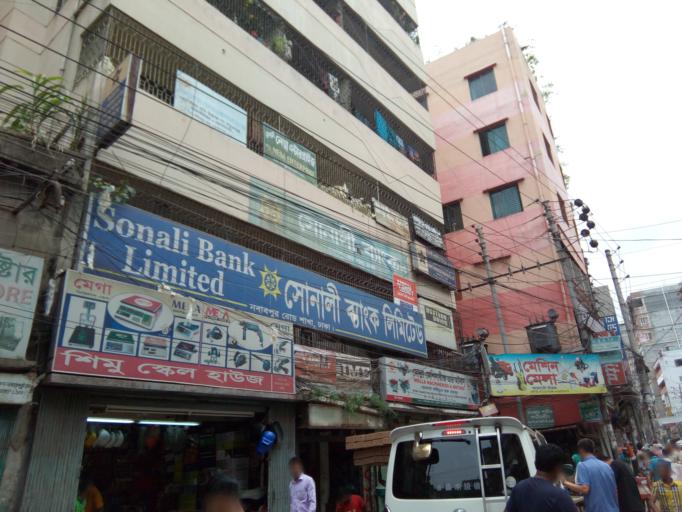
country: BD
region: Dhaka
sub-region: Dhaka
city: Dhaka
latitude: 23.7188
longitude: 90.4116
